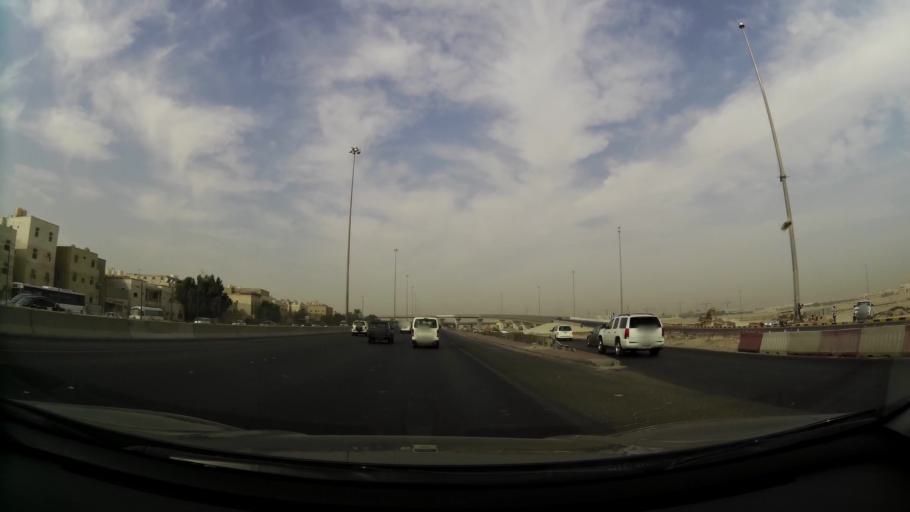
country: KW
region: Al Asimah
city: Ar Rabiyah
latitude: 29.2674
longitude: 47.9145
